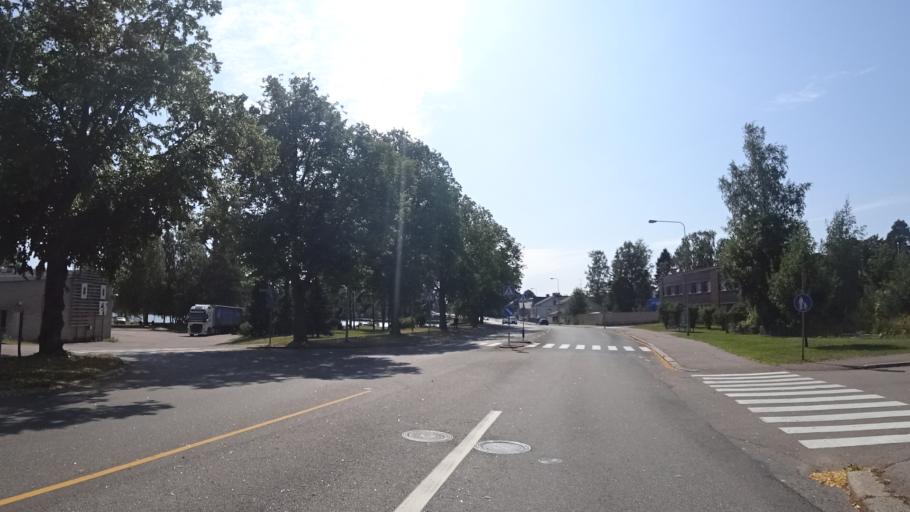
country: FI
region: Kymenlaakso
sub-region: Kotka-Hamina
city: Kotka
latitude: 60.4695
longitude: 26.9226
